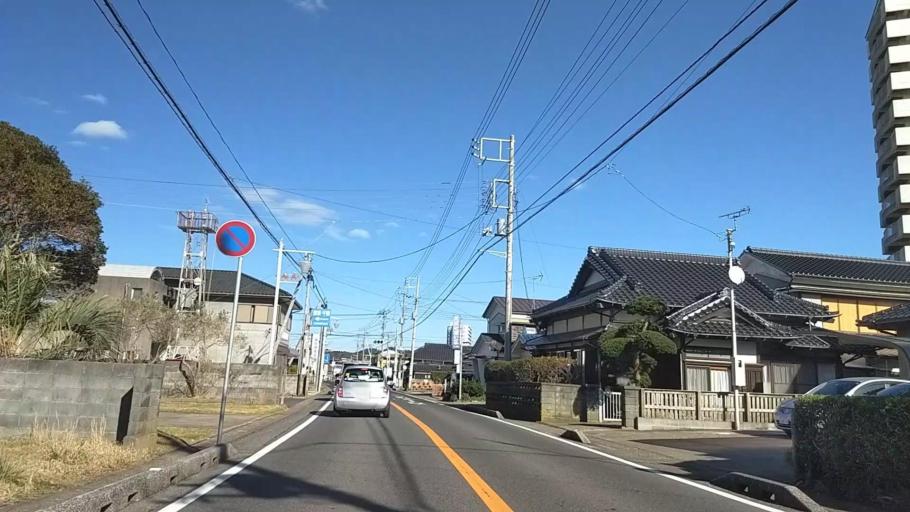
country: JP
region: Chiba
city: Katsuura
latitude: 35.1830
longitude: 140.3489
